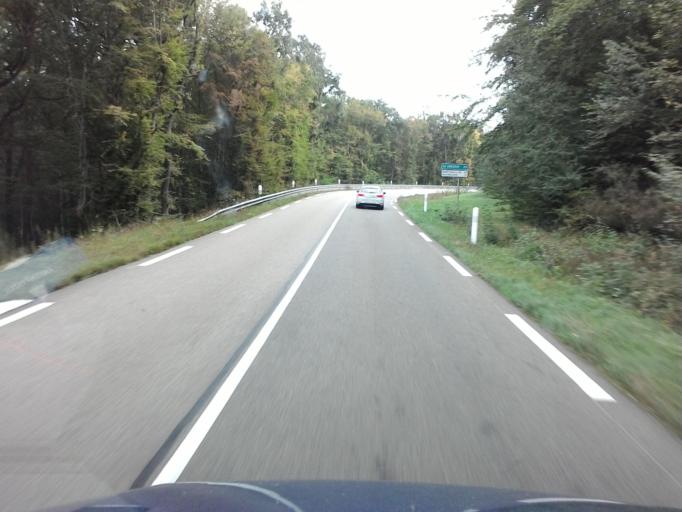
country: FR
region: Bourgogne
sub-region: Departement de Saone-et-Loire
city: Autun
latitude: 46.9479
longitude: 4.3486
